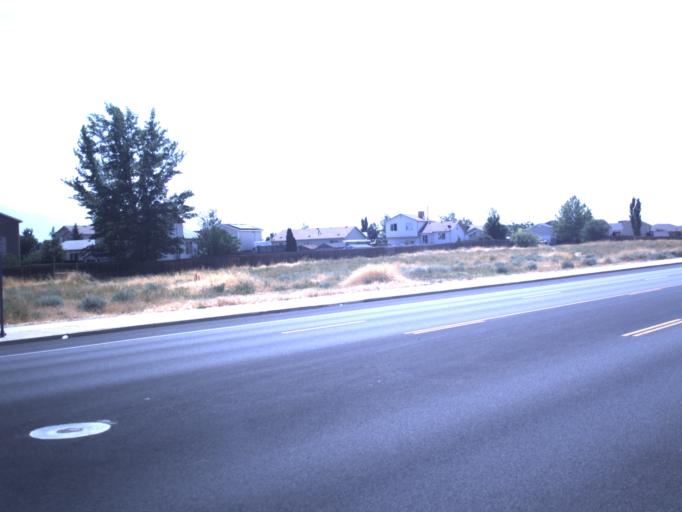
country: US
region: Utah
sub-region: Salt Lake County
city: Oquirrh
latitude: 40.6437
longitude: -112.0247
